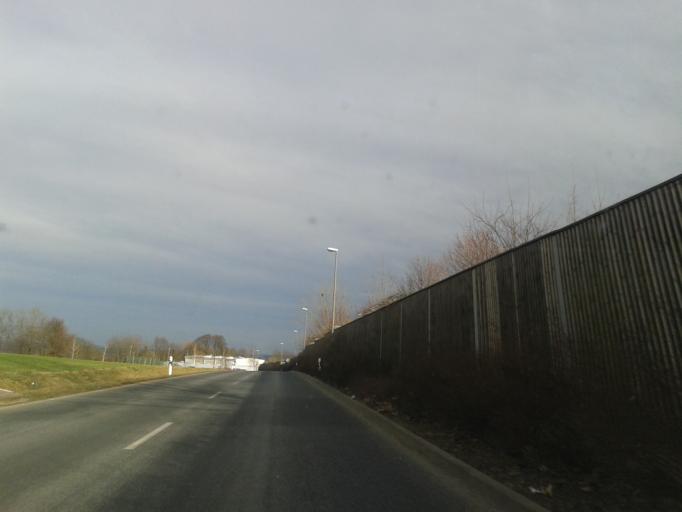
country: DE
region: Saxony
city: Freital
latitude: 51.0293
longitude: 13.6445
